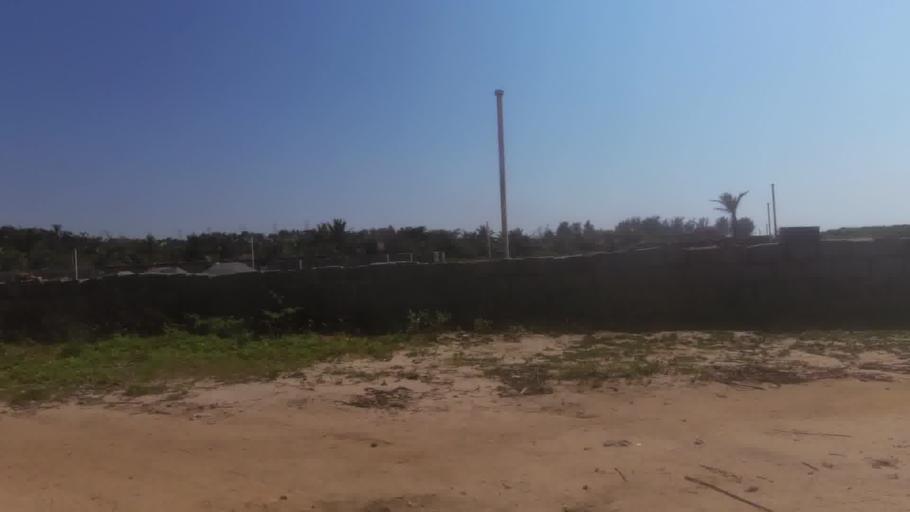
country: BR
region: Espirito Santo
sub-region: Marataizes
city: Marataizes
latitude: -21.0772
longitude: -40.8391
